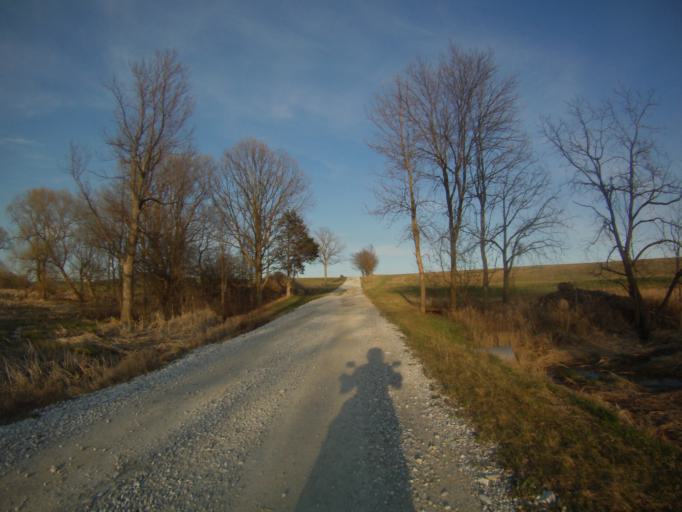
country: US
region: Vermont
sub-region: Addison County
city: Vergennes
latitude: 44.1008
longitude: -73.2760
